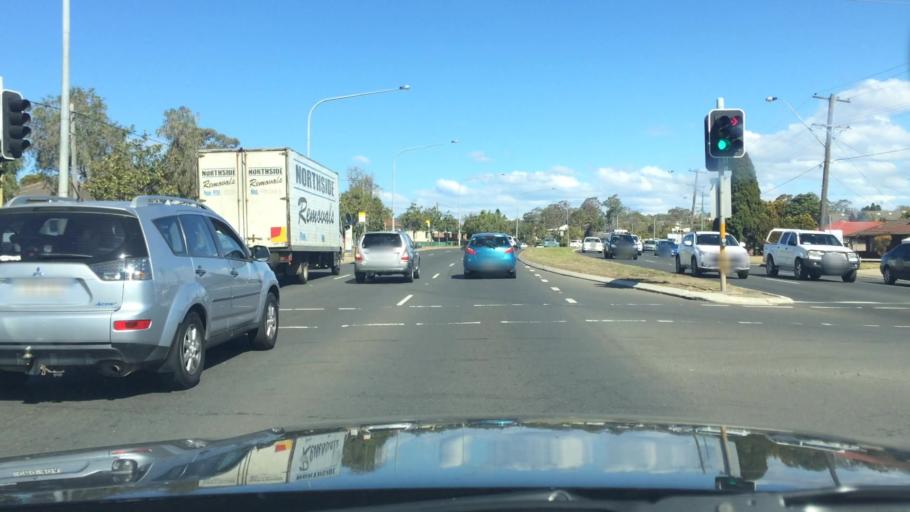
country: AU
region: New South Wales
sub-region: Campbelltown Municipality
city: Glenfield
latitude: -33.9436
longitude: 150.9112
